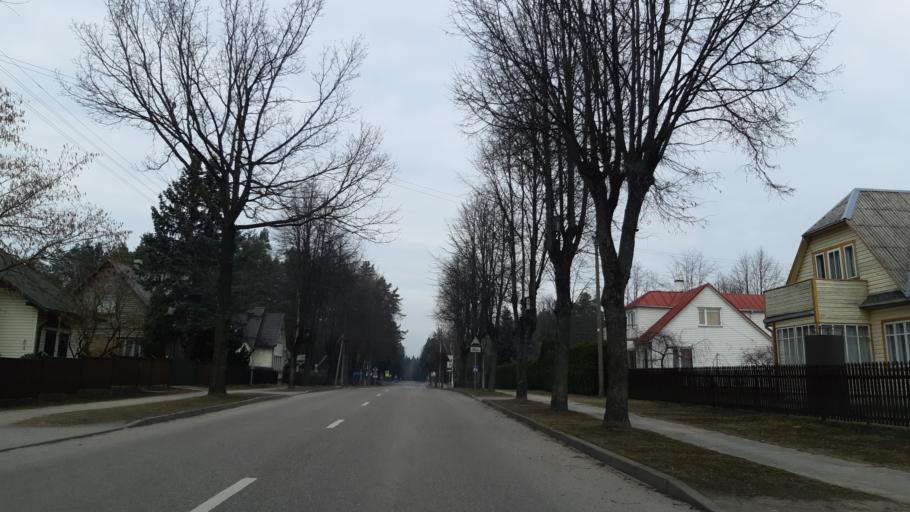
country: LT
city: Kazlu Ruda
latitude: 54.7551
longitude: 23.4968
